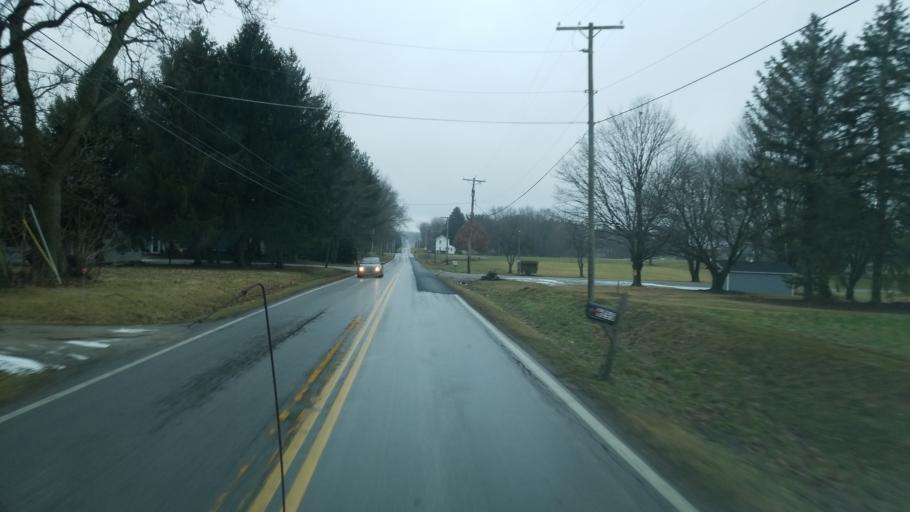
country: US
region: Ohio
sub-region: Wayne County
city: Smithville
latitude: 40.8590
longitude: -81.8248
